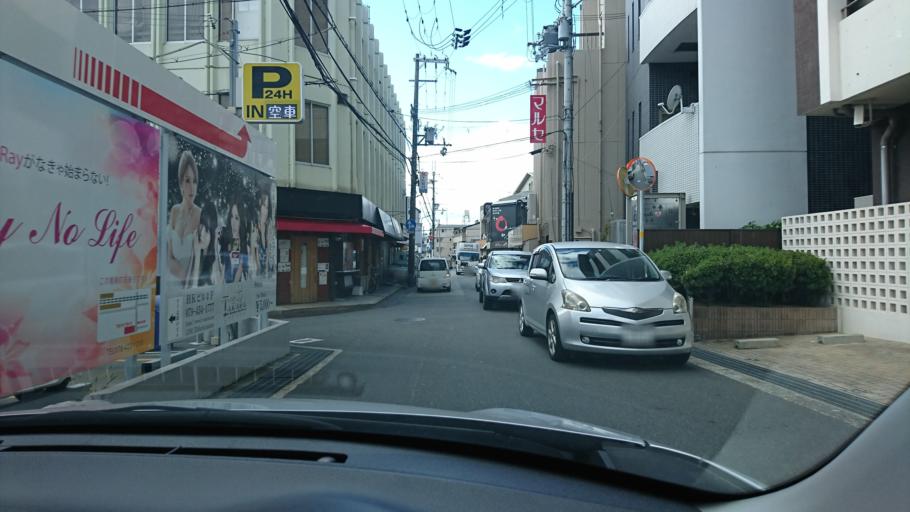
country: JP
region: Hyogo
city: Kakogawacho-honmachi
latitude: 34.7444
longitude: 134.8700
